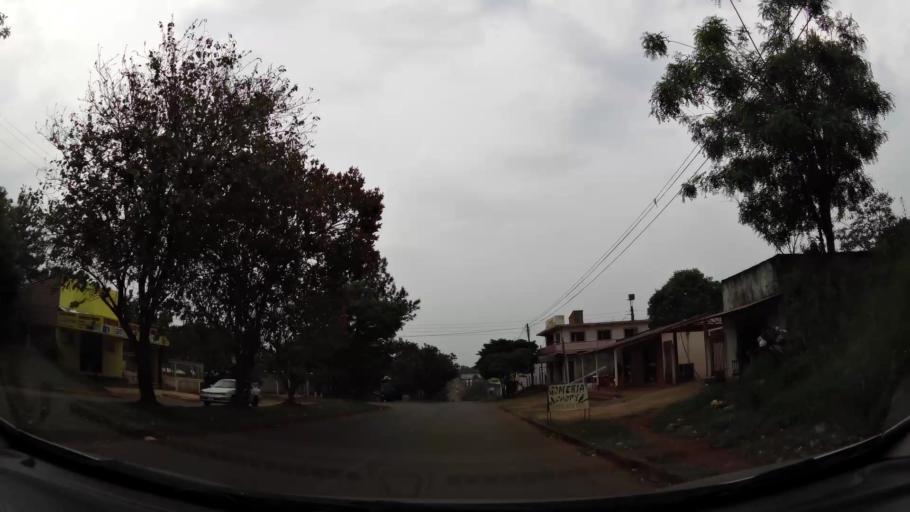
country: PY
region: Alto Parana
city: Presidente Franco
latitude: -25.5279
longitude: -54.6471
